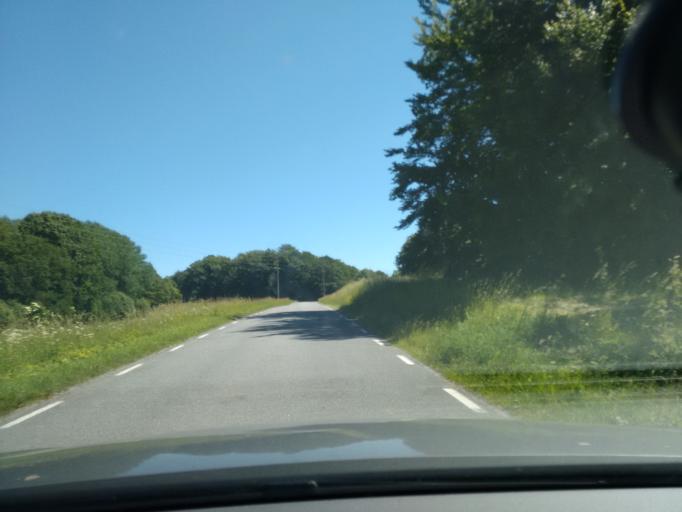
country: SE
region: Skane
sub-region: Kristianstads Kommun
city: Degeberga
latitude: 55.7787
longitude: 14.0281
